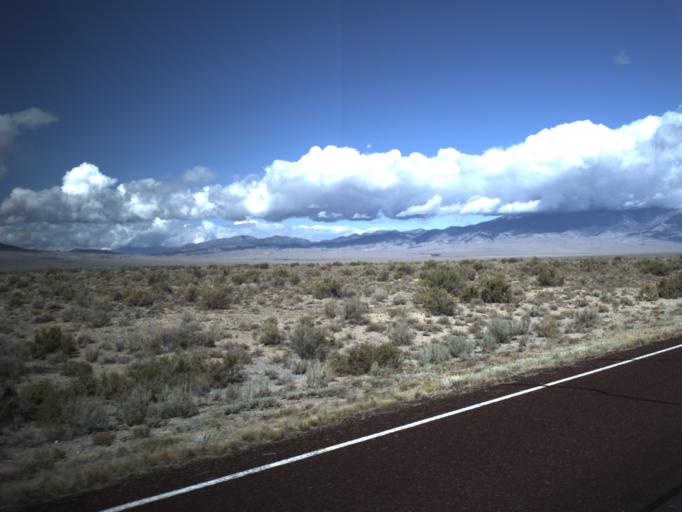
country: US
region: Nevada
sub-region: White Pine County
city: McGill
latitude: 38.9525
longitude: -114.0333
